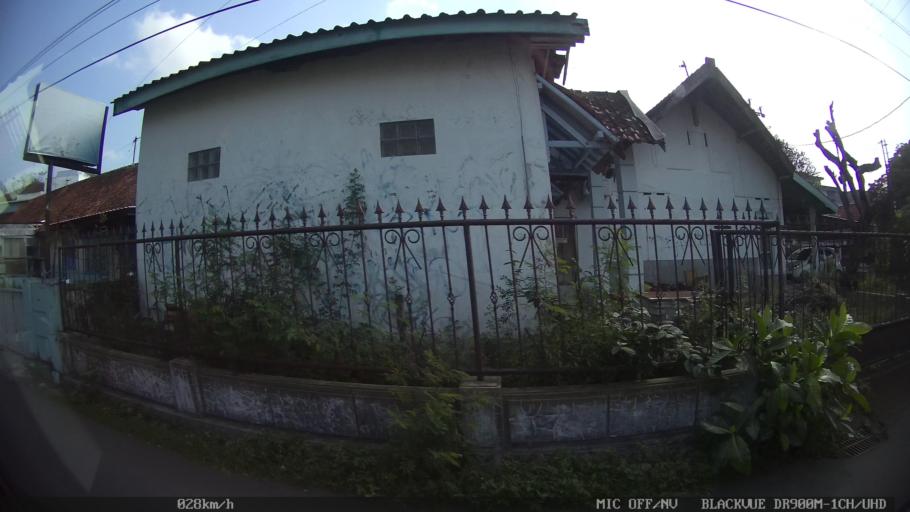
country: ID
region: Daerah Istimewa Yogyakarta
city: Yogyakarta
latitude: -7.7769
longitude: 110.3919
